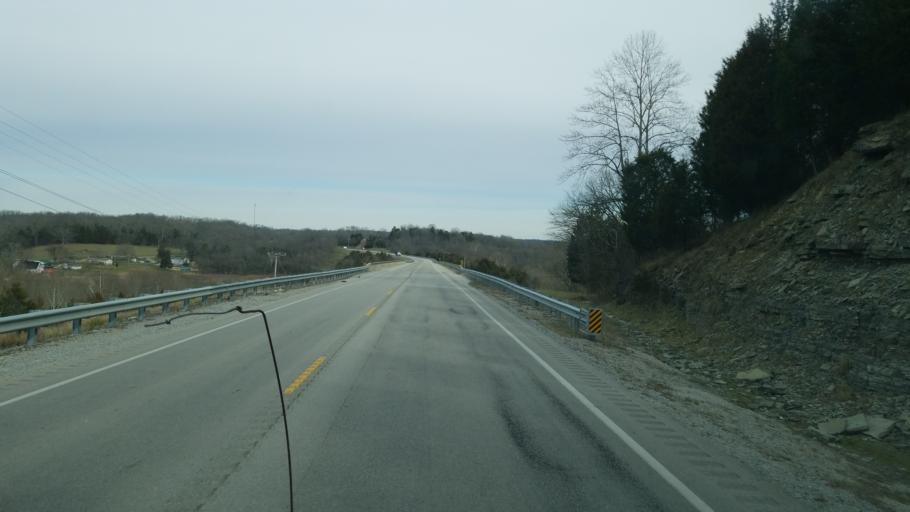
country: US
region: Kentucky
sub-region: Nicholas County
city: Carlisle
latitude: 38.4190
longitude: -83.9990
